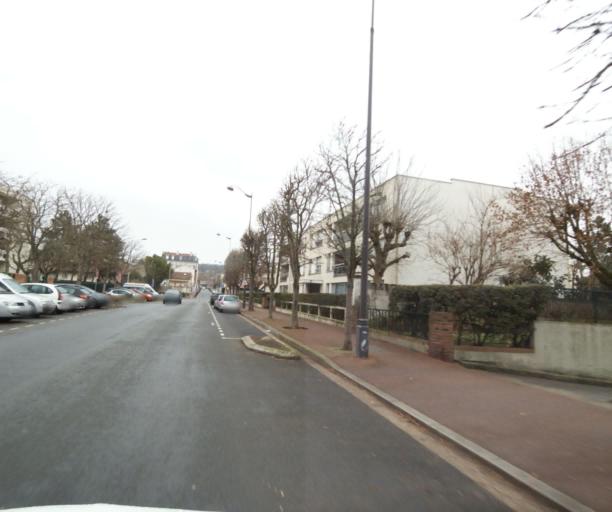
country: FR
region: Ile-de-France
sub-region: Departement des Hauts-de-Seine
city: Rueil-Malmaison
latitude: 48.8861
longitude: 2.1886
